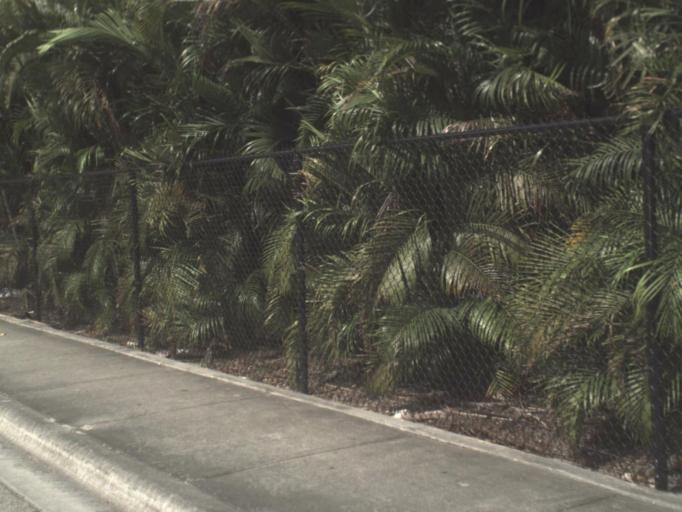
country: US
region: Florida
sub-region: Miami-Dade County
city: Doral
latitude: 25.8113
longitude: -80.3453
